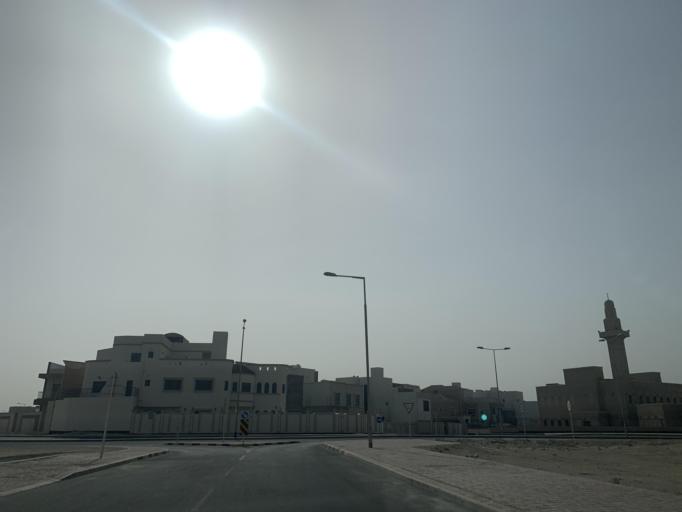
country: BH
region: Northern
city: Madinat `Isa
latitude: 26.1631
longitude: 50.5398
